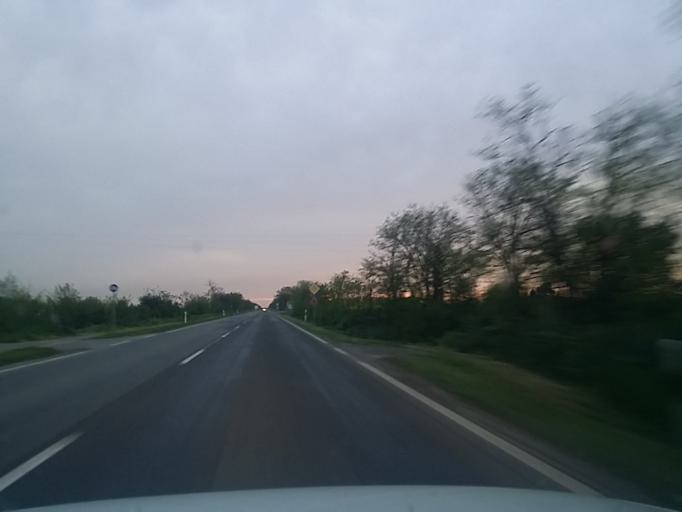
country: HU
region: Bekes
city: Mezobereny
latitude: 46.7098
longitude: 20.9793
